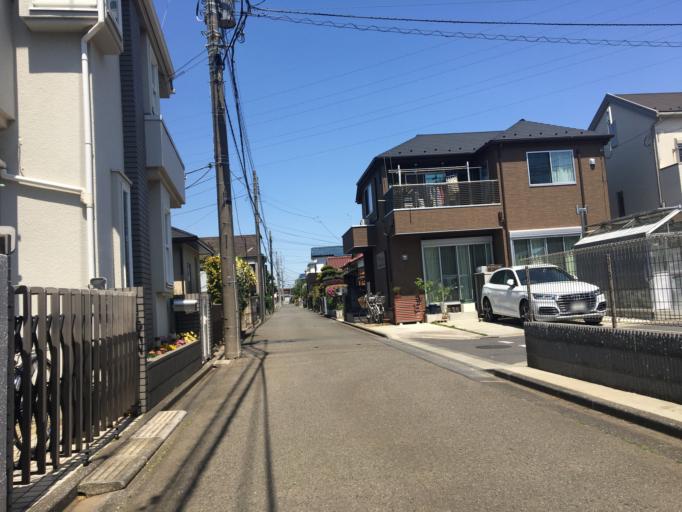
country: JP
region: Tokyo
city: Tanashicho
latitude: 35.7208
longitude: 139.5084
